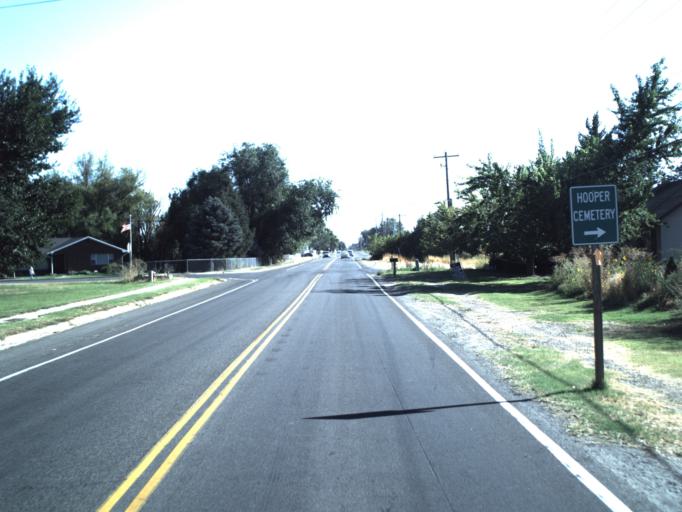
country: US
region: Utah
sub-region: Weber County
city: Hooper
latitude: 41.1721
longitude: -112.1227
